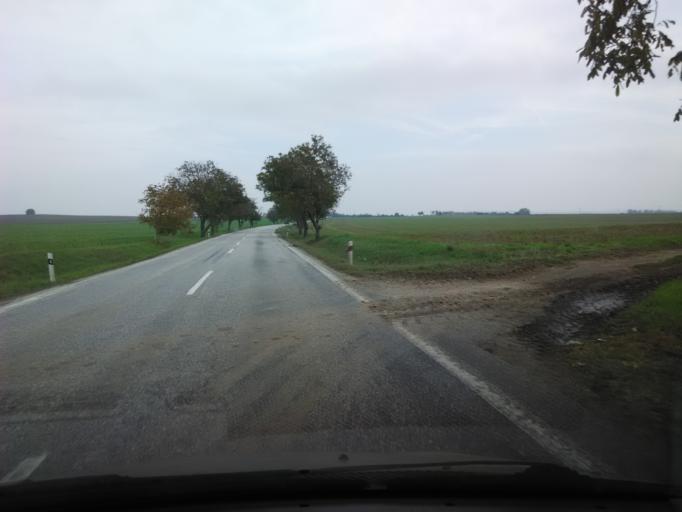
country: SK
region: Nitriansky
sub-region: Okres Nove Zamky
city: Nove Zamky
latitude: 47.9924
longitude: 18.3139
